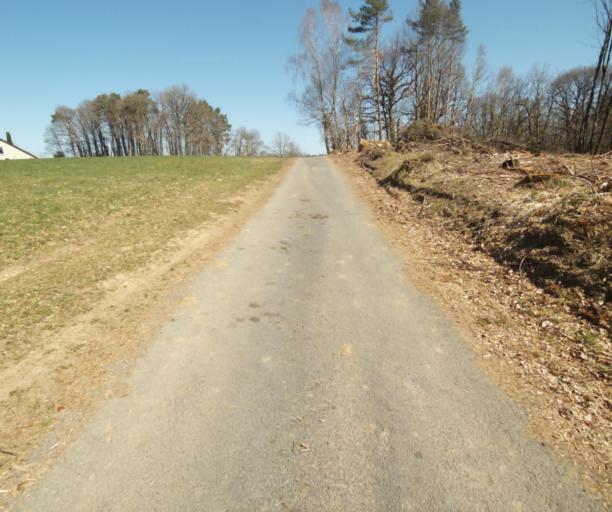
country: FR
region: Limousin
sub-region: Departement de la Correze
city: Saint-Mexant
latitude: 45.3044
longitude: 1.6387
